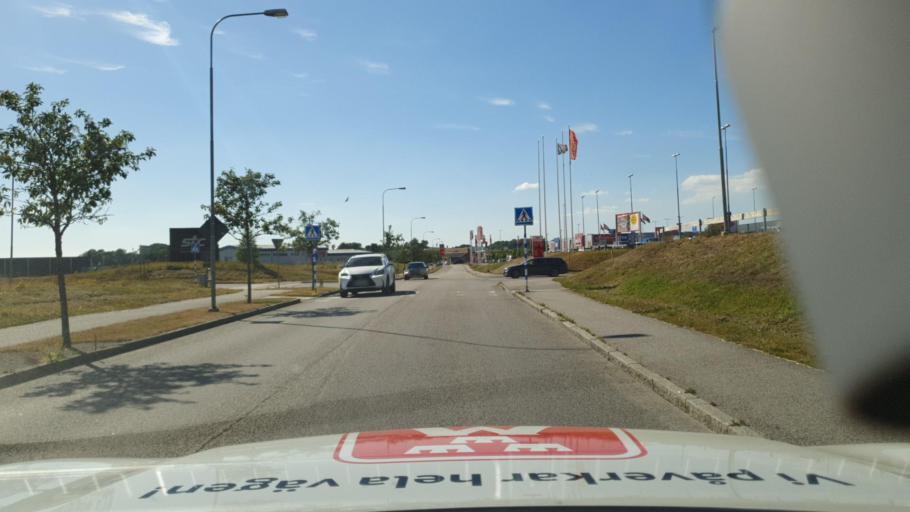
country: SE
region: Skane
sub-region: Skurups Kommun
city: Skurup
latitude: 55.4892
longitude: 13.4881
